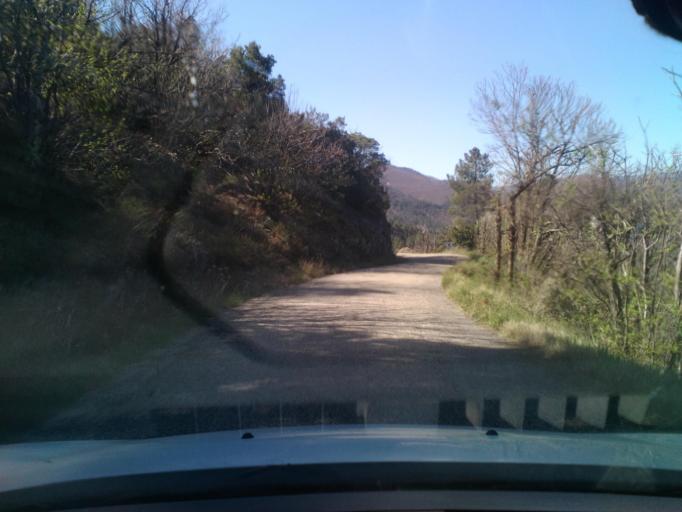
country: FR
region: Languedoc-Roussillon
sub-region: Departement du Gard
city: Saint-Jean-du-Gard
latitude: 44.1378
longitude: 3.7638
